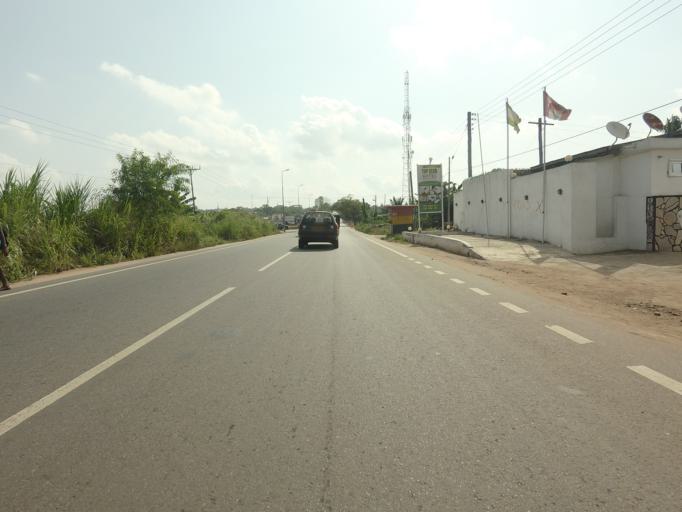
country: GH
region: Volta
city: Ho
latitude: 6.6026
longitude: 0.4893
